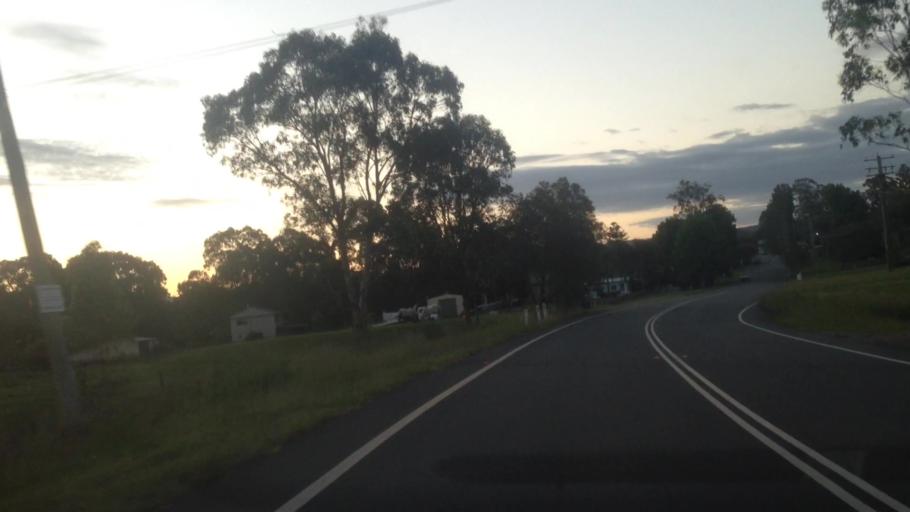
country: AU
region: New South Wales
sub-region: Lake Macquarie Shire
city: Cooranbong
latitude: -33.0717
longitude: 151.4675
